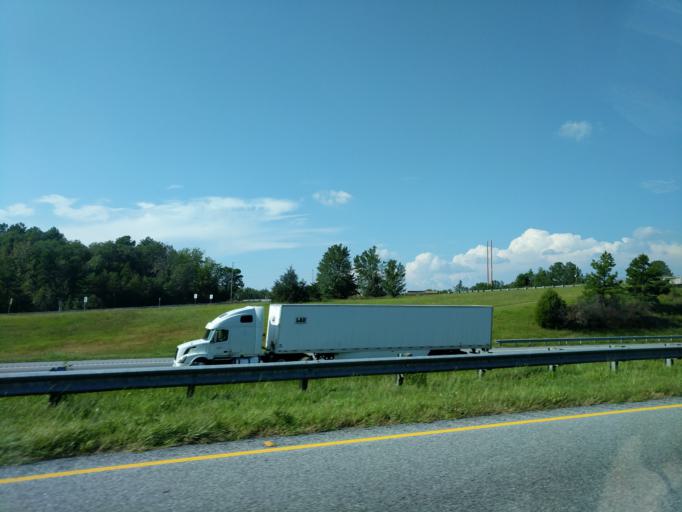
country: US
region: Georgia
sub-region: Franklin County
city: Gumlog
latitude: 34.4893
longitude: -83.0228
